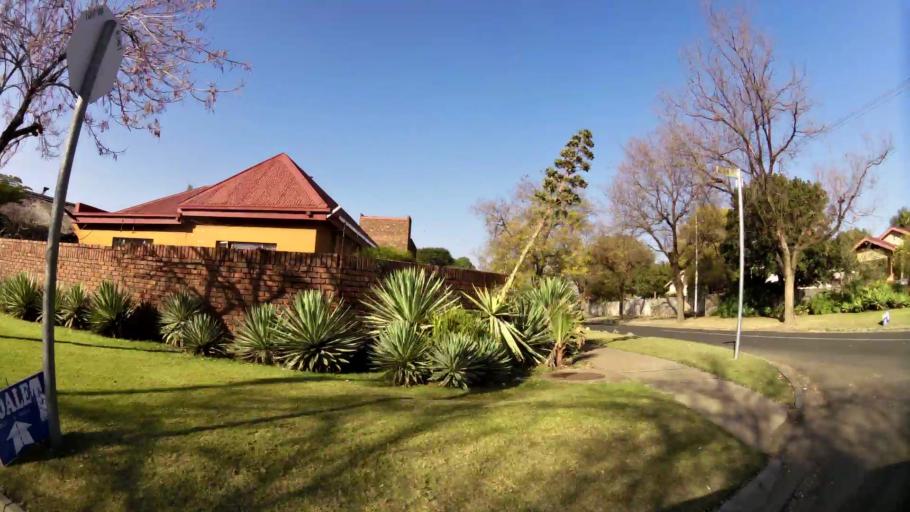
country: ZA
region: Gauteng
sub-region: City of Tshwane Metropolitan Municipality
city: Pretoria
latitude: -25.7211
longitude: 28.1520
